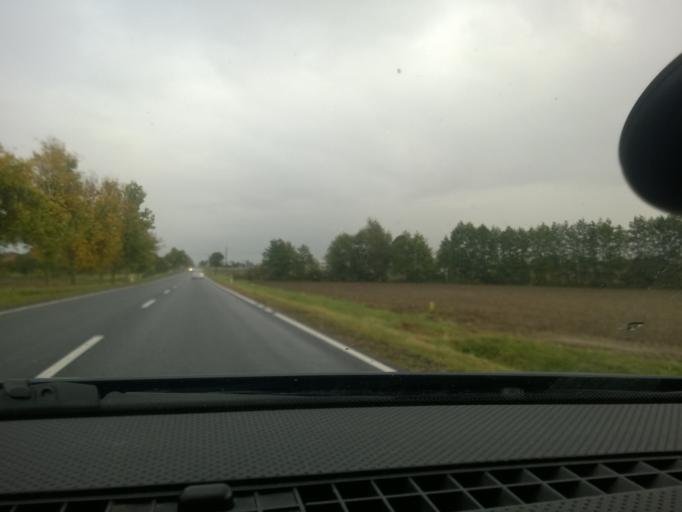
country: PL
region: Lodz Voivodeship
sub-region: Powiat sieradzki
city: Blaszki
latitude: 51.6775
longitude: 18.3522
